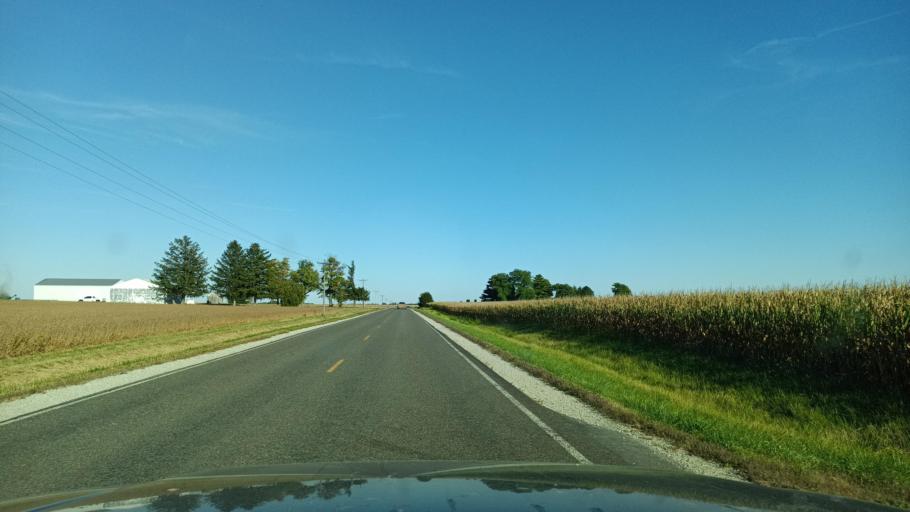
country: US
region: Illinois
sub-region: De Witt County
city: Clinton
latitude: 40.2244
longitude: -88.8780
